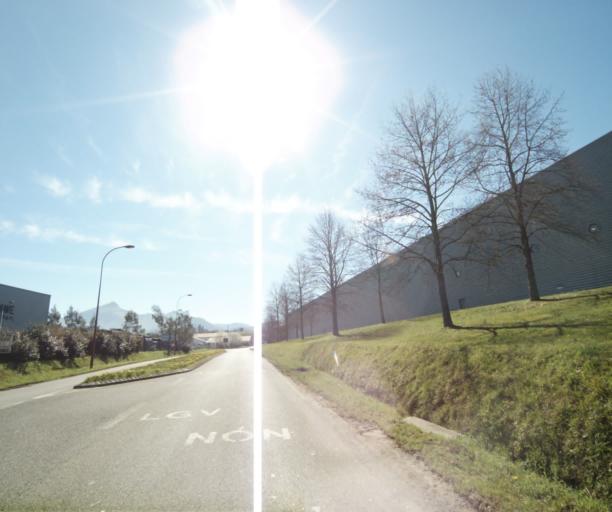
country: FR
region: Aquitaine
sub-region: Departement des Pyrenees-Atlantiques
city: Urrugne
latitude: 43.3531
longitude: -1.6899
